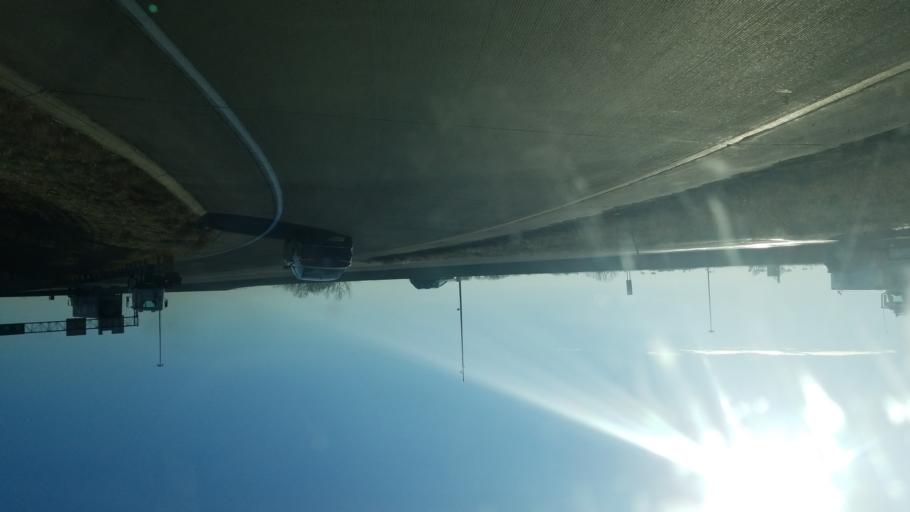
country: US
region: Iowa
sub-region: Woodbury County
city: Sergeant Bluff
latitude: 42.4464
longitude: -96.3737
